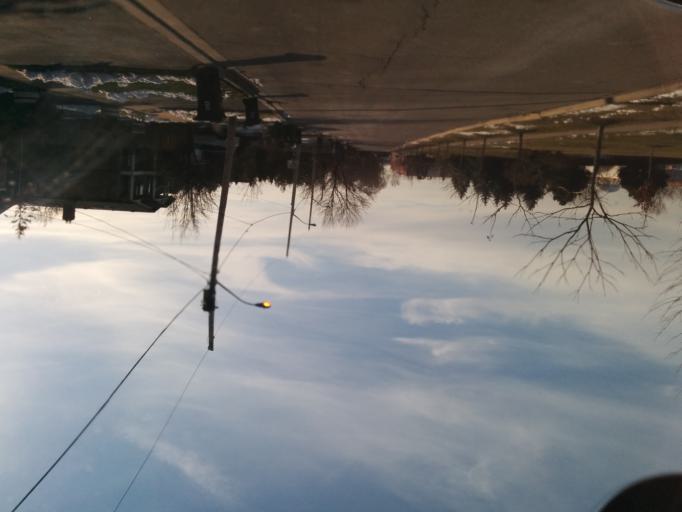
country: CA
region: Ontario
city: Etobicoke
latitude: 43.6095
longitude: -79.5299
